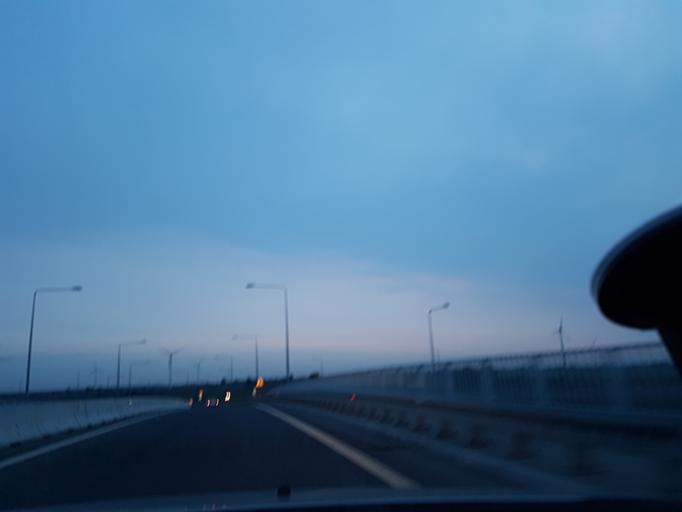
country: PL
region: Lodz Voivodeship
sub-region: Powiat kutnowski
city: Krzyzanow
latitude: 52.2189
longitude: 19.4684
